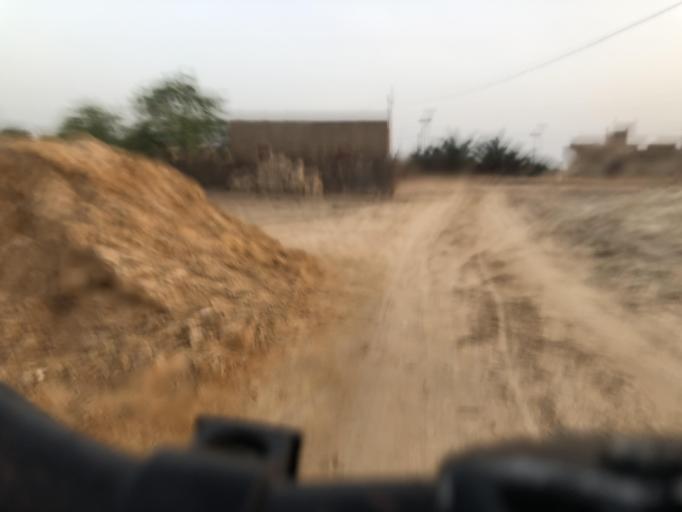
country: SN
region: Saint-Louis
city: Saint-Louis
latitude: 16.0702
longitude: -16.4315
